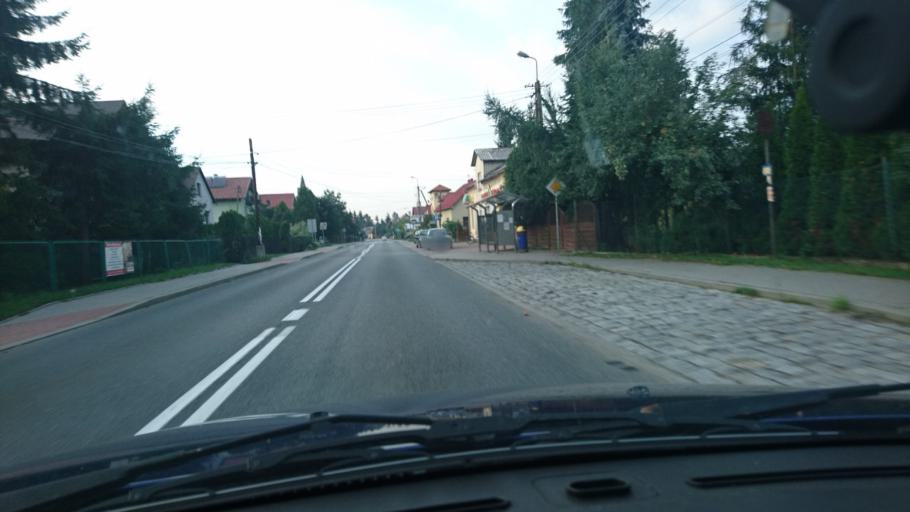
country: PL
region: Silesian Voivodeship
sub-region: Powiat zywiecki
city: Cisiec
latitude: 49.5829
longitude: 19.1018
